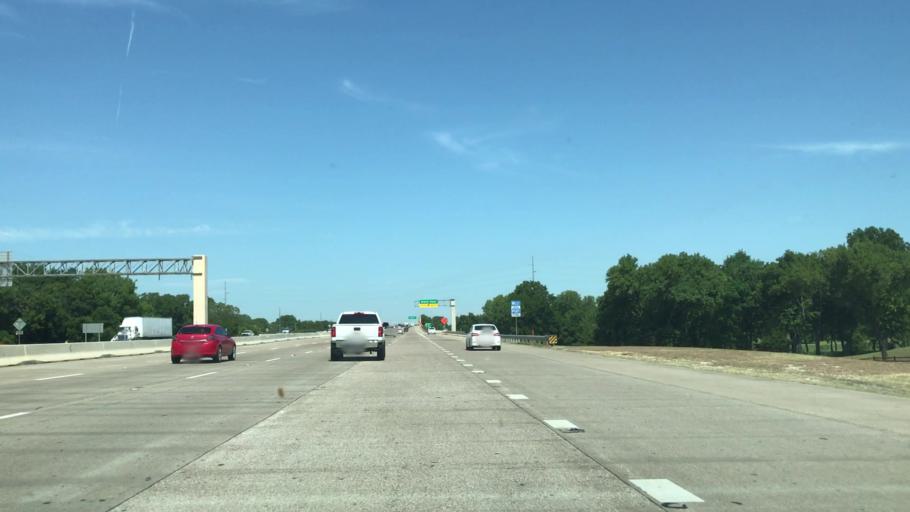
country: US
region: Texas
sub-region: Dallas County
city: Sachse
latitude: 32.9535
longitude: -96.6236
